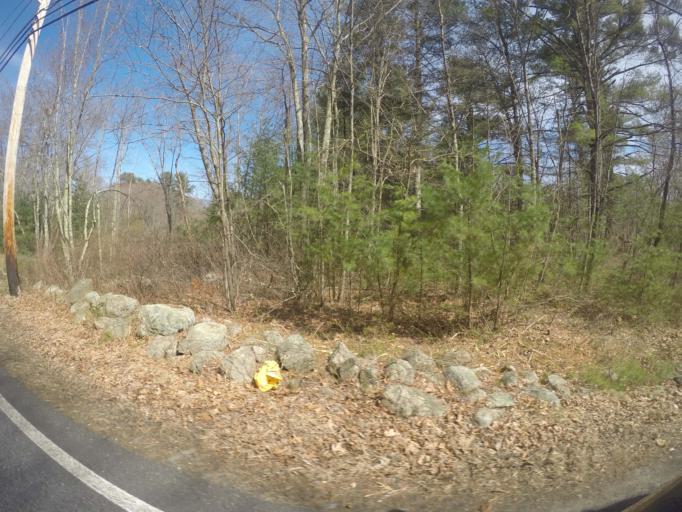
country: US
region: Massachusetts
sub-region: Bristol County
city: Easton
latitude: 42.0202
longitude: -71.0949
